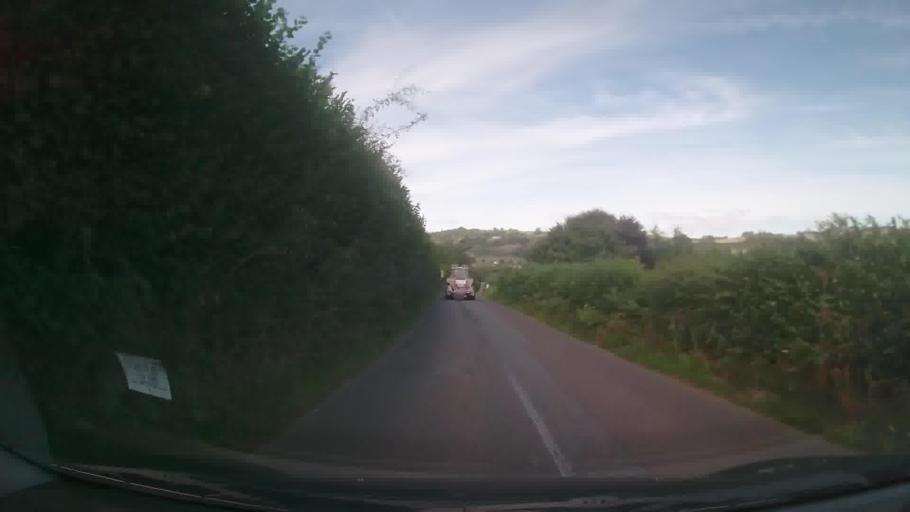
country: GB
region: Wales
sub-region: Sir Powys
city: Whitton
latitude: 52.2941
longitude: -3.0746
